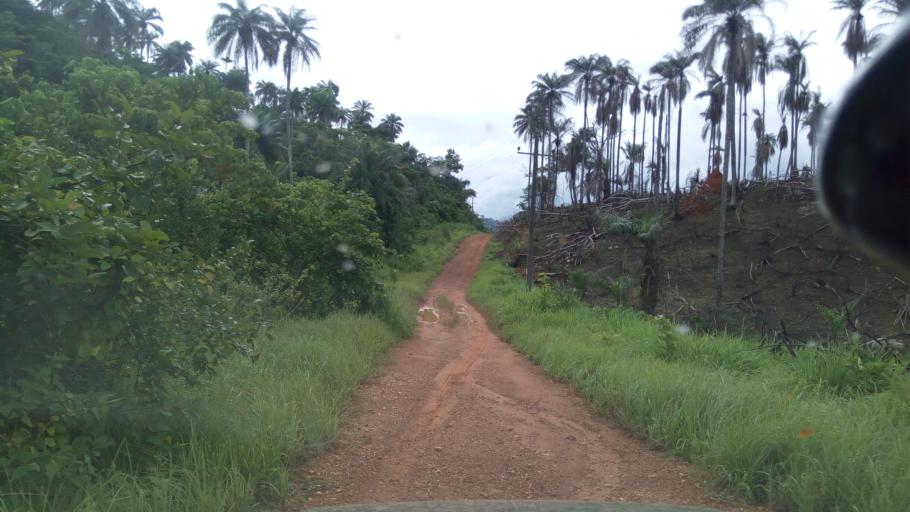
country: SL
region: Eastern Province
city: Boajibu
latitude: 8.1518
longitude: -11.2575
